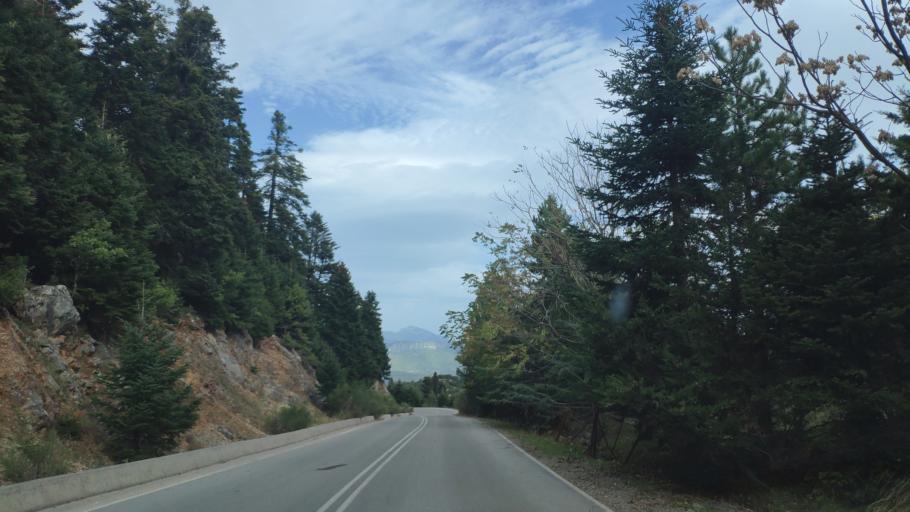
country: GR
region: Central Greece
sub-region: Nomos Fokidos
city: Amfissa
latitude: 38.6571
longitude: 22.3823
